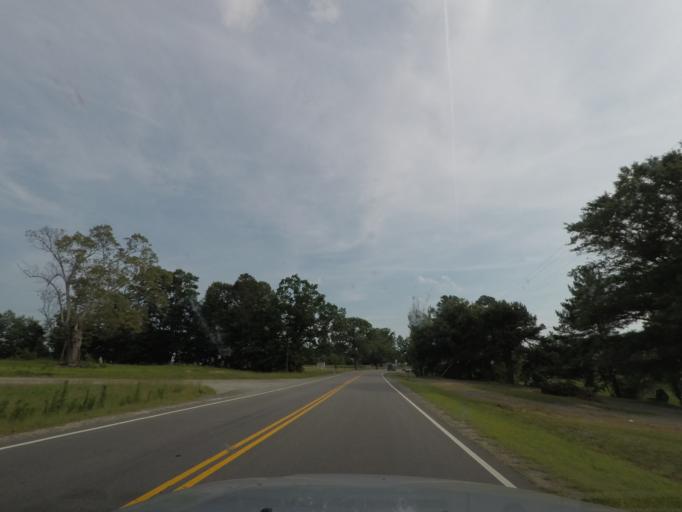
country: US
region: Virginia
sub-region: Mecklenburg County
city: Chase City
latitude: 36.8589
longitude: -78.5894
